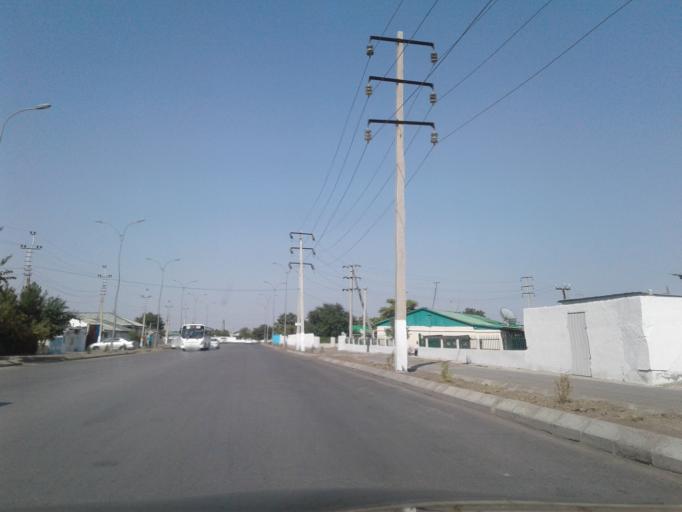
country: TM
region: Ahal
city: Ashgabat
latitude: 37.9740
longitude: 58.4318
